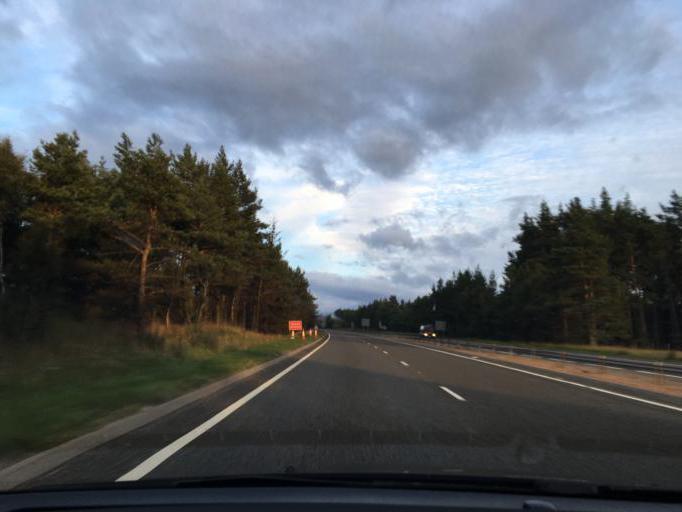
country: GB
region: Scotland
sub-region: Highland
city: Aviemore
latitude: 57.3429
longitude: -3.9971
